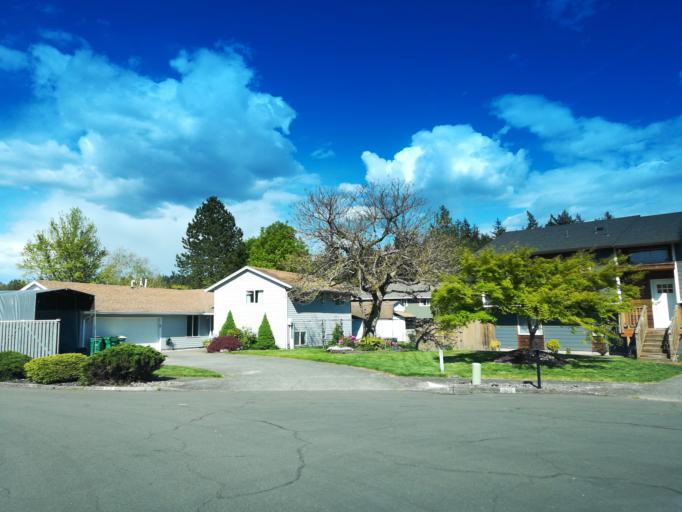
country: US
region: Oregon
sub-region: Multnomah County
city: Troutdale
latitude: 45.5279
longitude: -122.3825
